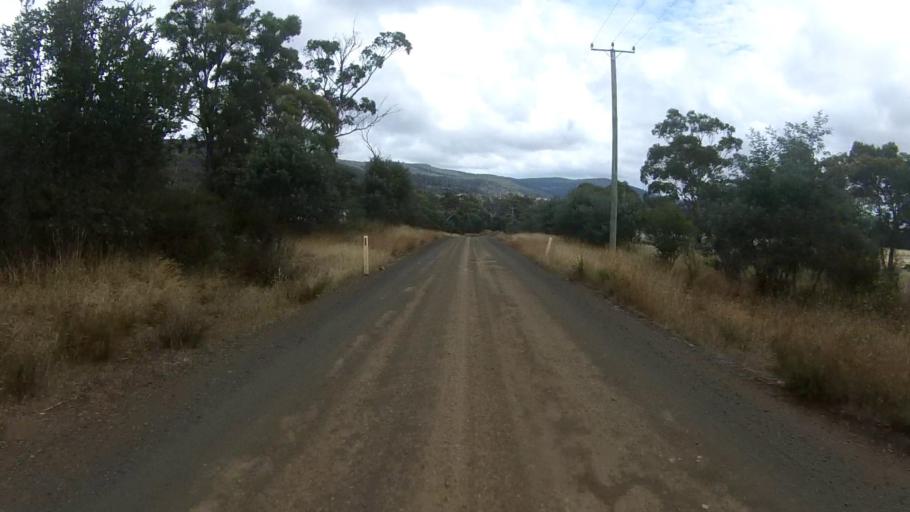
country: AU
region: Tasmania
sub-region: Break O'Day
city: St Helens
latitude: -41.8232
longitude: 147.9868
